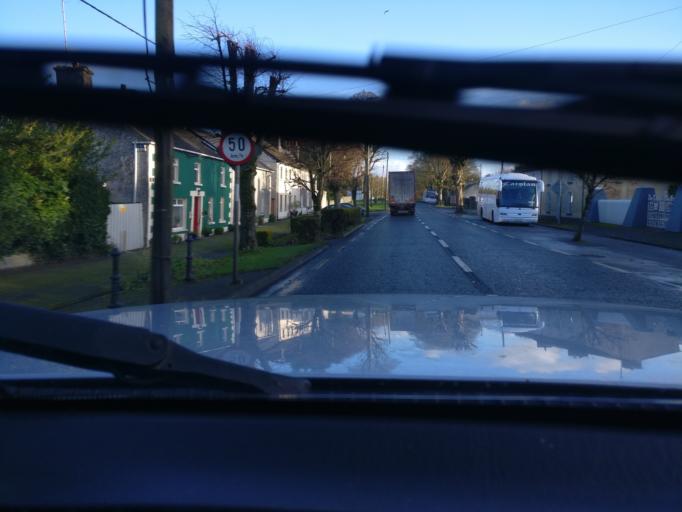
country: IE
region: Leinster
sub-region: An Mhi
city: Athboy
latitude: 53.6633
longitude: -7.0129
